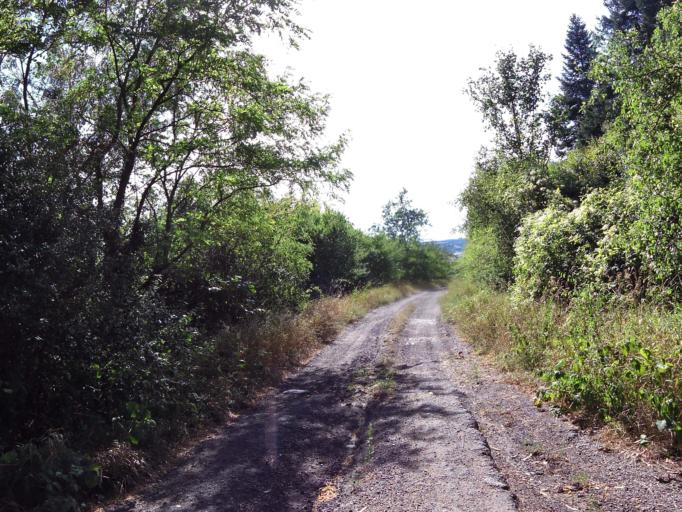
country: DE
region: Bavaria
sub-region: Regierungsbezirk Unterfranken
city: Eibelstadt
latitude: 49.7418
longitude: 10.0117
